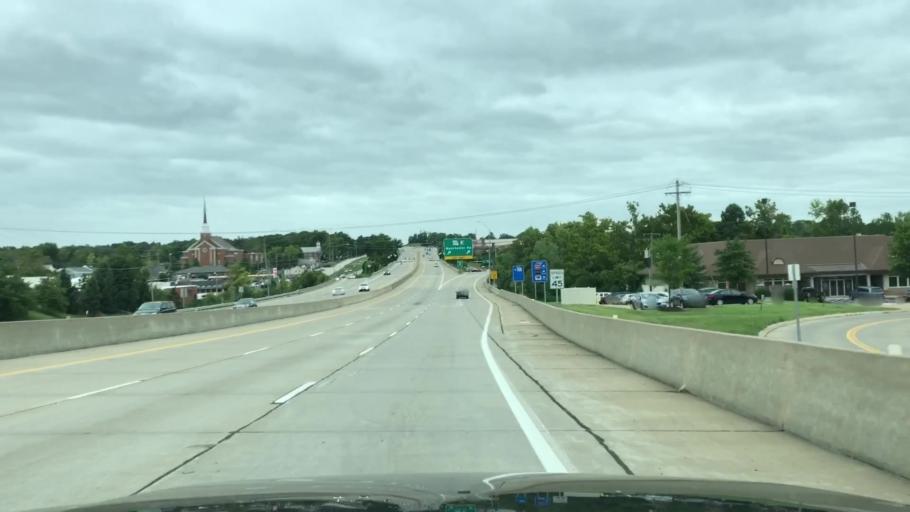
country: US
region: Missouri
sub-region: Saint Louis County
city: Manchester
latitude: 38.5884
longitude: -90.5086
